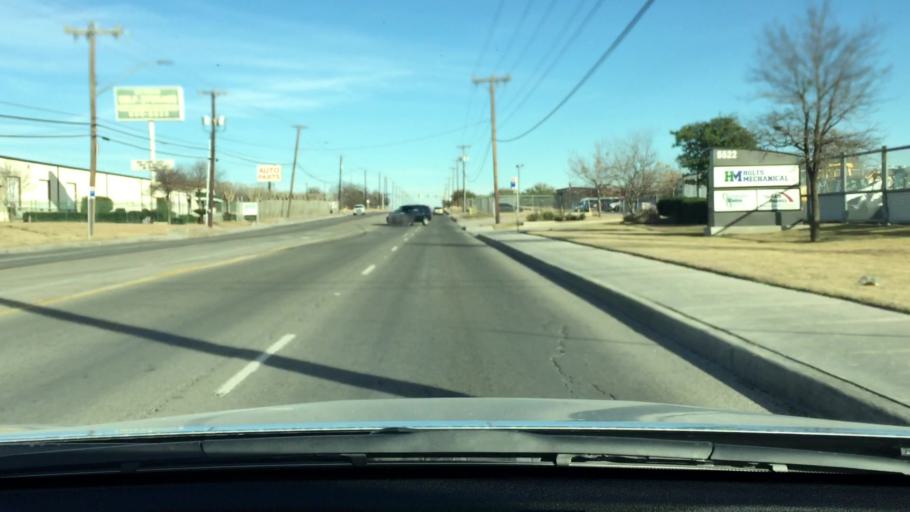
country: US
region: Texas
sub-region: Bexar County
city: Kirby
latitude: 29.4841
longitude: -98.3811
